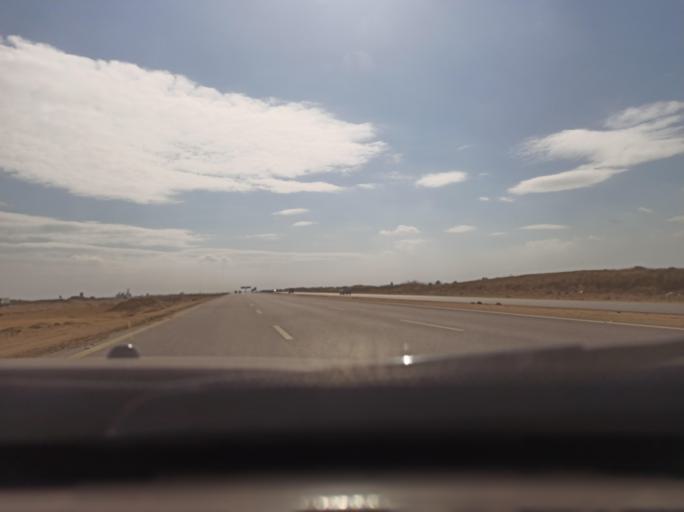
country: EG
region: Muhafazat al Fayyum
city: Tamiyah
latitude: 29.5595
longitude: 31.0588
